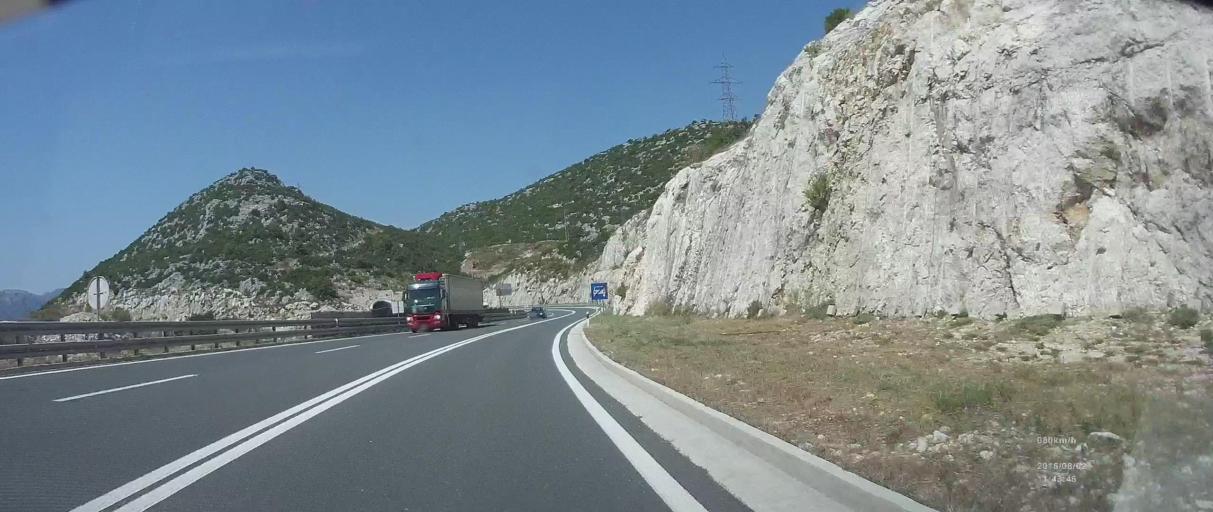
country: HR
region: Dubrovacko-Neretvanska
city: Komin
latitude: 43.0545
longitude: 17.4661
